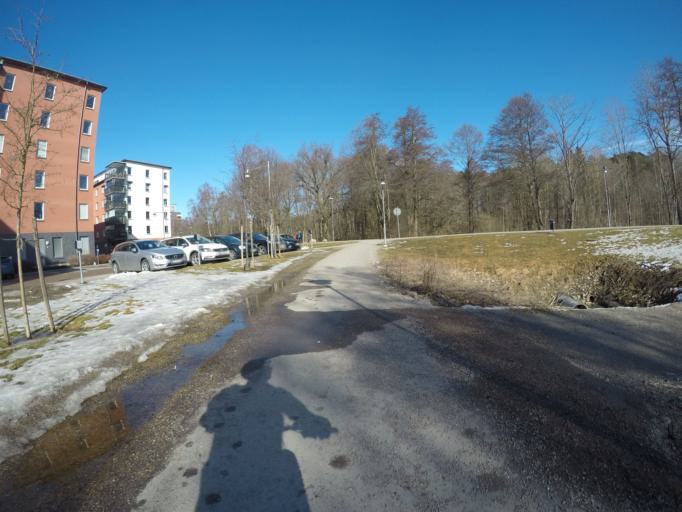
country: SE
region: Vaestmanland
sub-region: Vasteras
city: Vasteras
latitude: 59.6013
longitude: 16.5807
